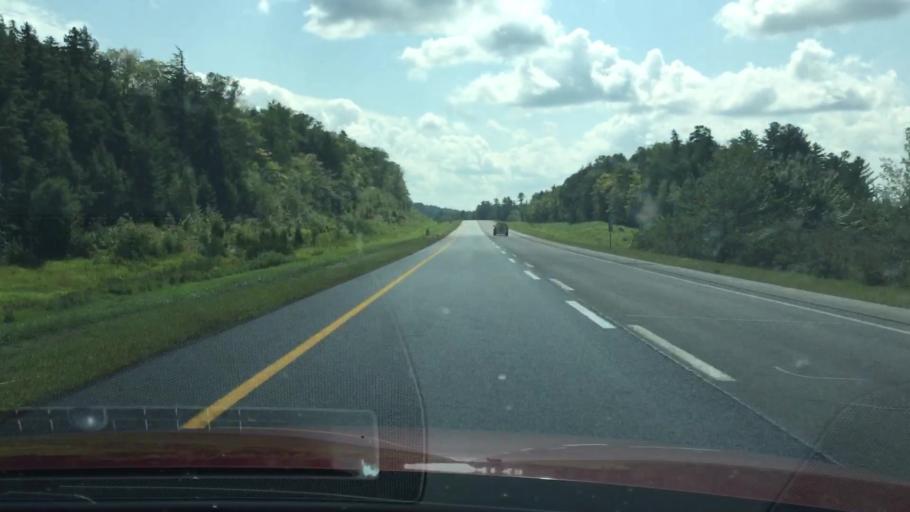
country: US
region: Maine
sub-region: Penobscot County
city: Medway
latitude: 45.7248
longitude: -68.4741
